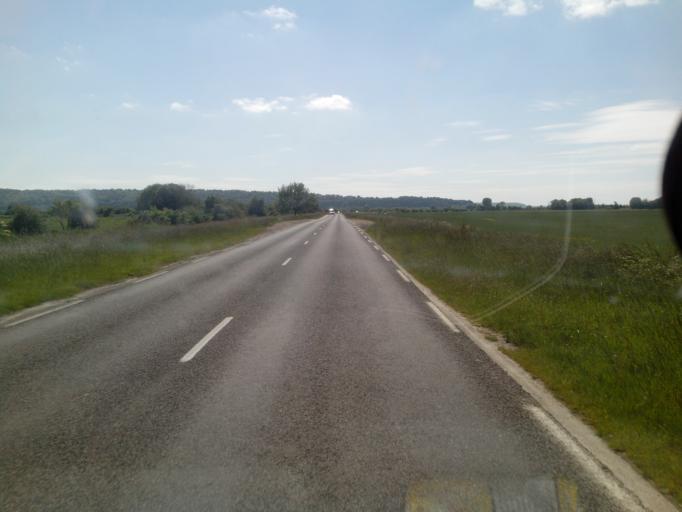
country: FR
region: Haute-Normandie
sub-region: Departement de la Seine-Maritime
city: Tancarville
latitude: 49.4557
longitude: 0.4692
